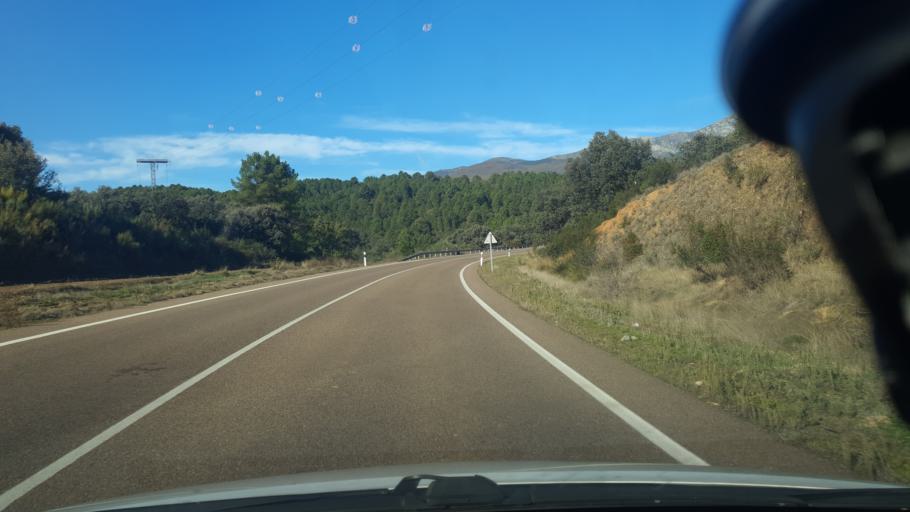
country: ES
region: Castille and Leon
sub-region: Provincia de Avila
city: Poyales del Hoyo
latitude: 40.1632
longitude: -5.1178
